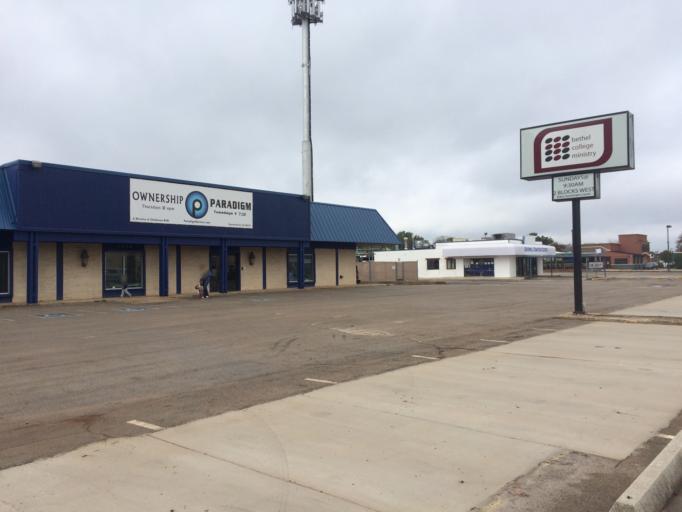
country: US
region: Oklahoma
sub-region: Cleveland County
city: Norman
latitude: 35.2038
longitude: -97.4617
